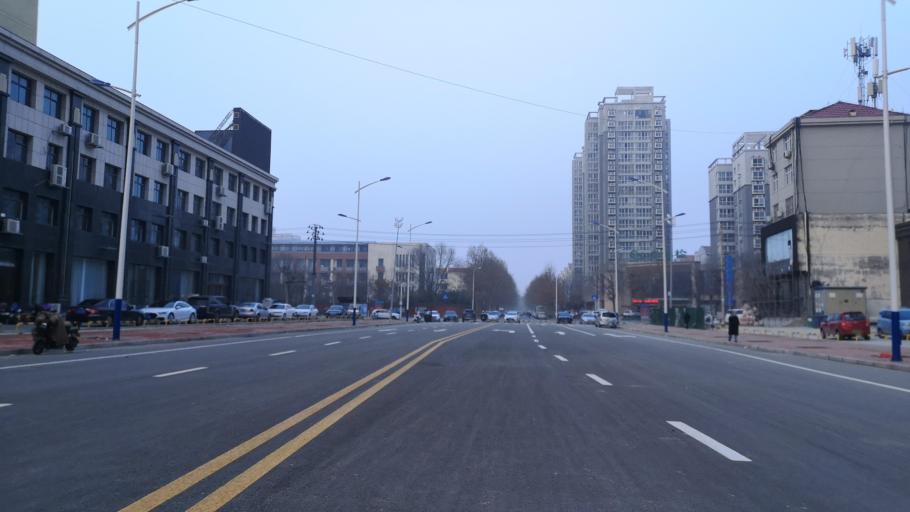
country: CN
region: Henan Sheng
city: Zhongyuanlu
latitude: 35.7522
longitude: 115.0604
